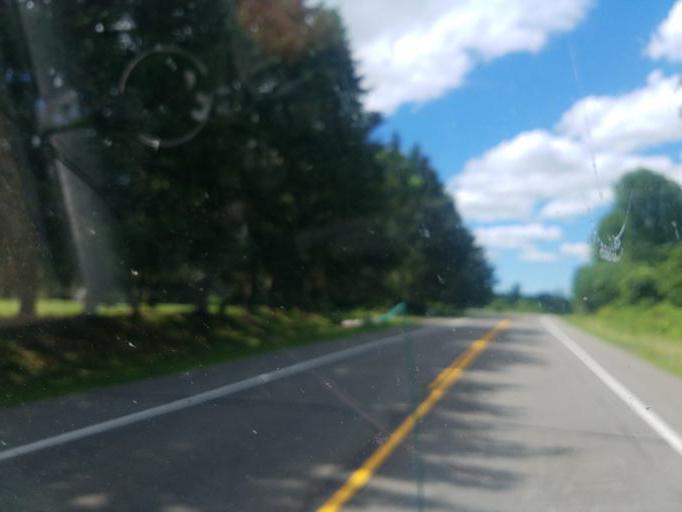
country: US
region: New York
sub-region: Wayne County
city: Lyons
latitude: 42.9826
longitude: -76.9782
